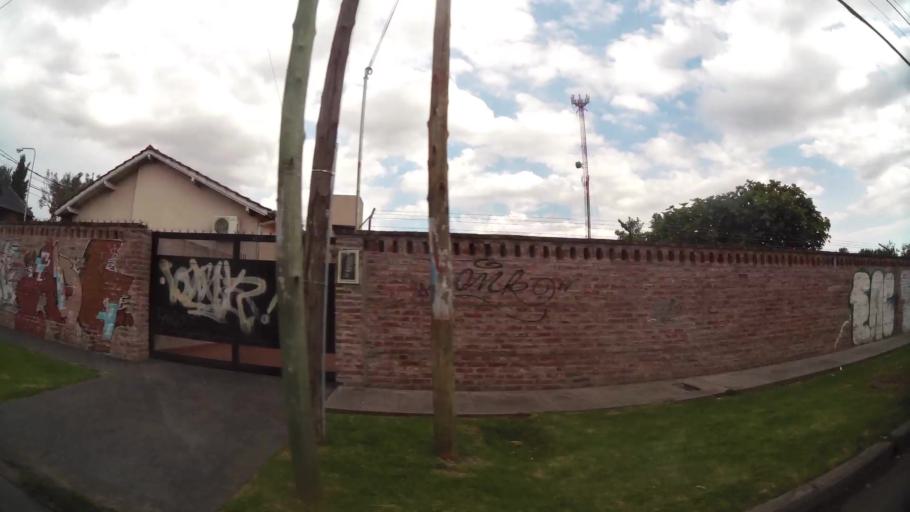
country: AR
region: Buenos Aires
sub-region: Partido de Tigre
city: Tigre
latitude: -34.4672
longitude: -58.6527
